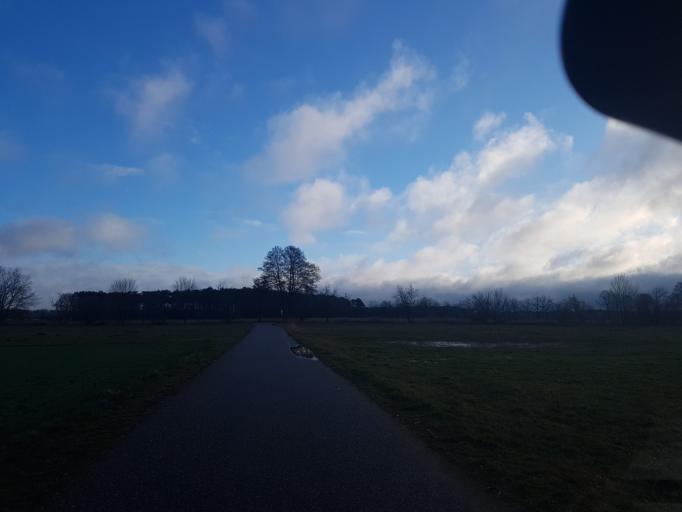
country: DE
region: Brandenburg
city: Ruckersdorf
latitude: 51.5965
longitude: 13.6230
